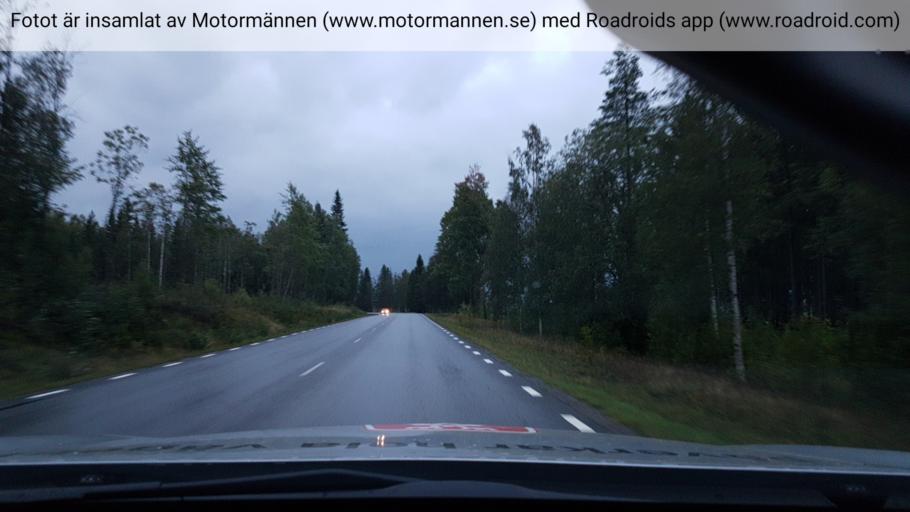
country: SE
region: Vaesterbotten
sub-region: Umea Kommun
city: Ersmark
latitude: 63.8598
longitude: 20.2994
